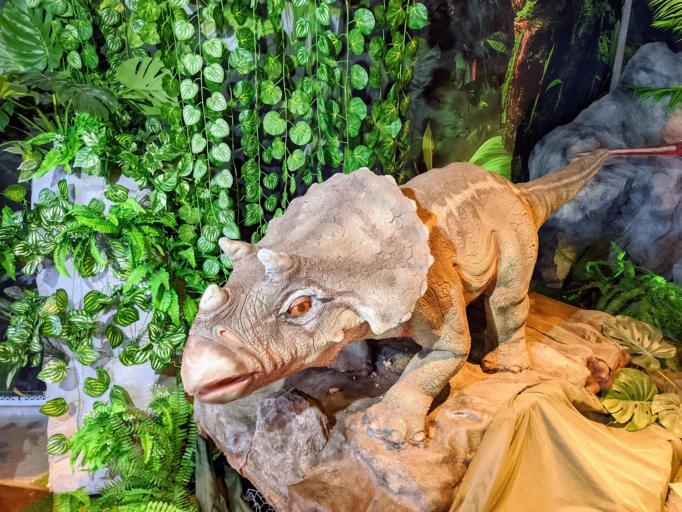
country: NO
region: Ostfold
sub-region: Sarpsborg
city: Sarpsborg
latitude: 59.2980
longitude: 11.0619
